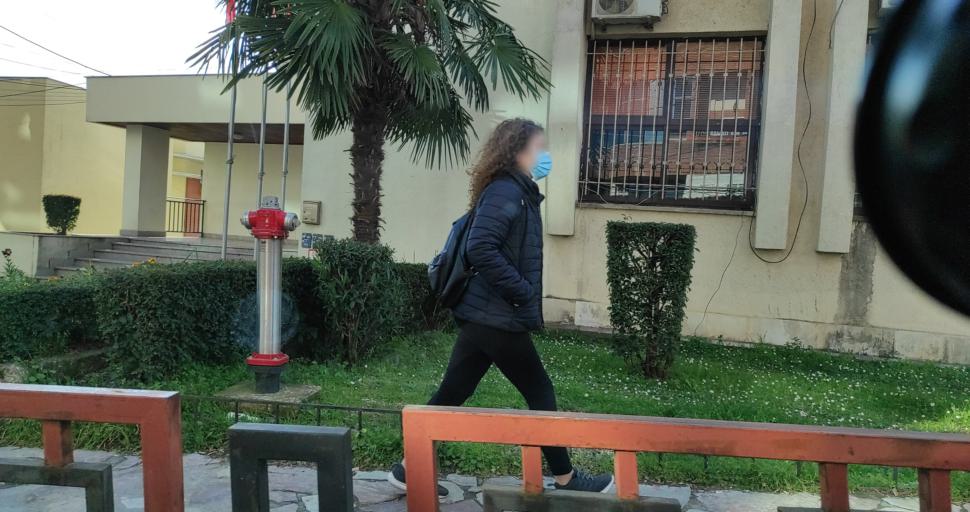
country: AL
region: Lezhe
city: Lezhe
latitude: 41.7818
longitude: 19.6440
